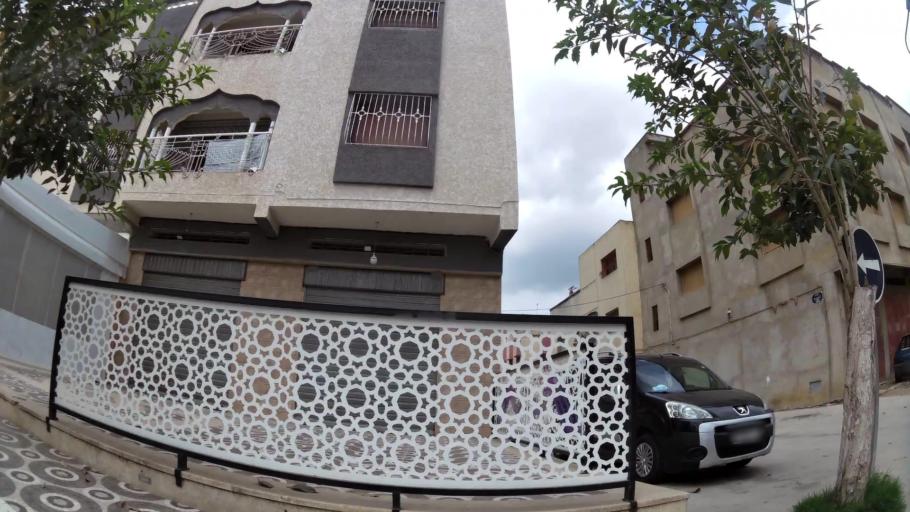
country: MA
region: Rabat-Sale-Zemmour-Zaer
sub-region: Khemisset
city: Tiflet
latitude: 33.8914
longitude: -6.3212
